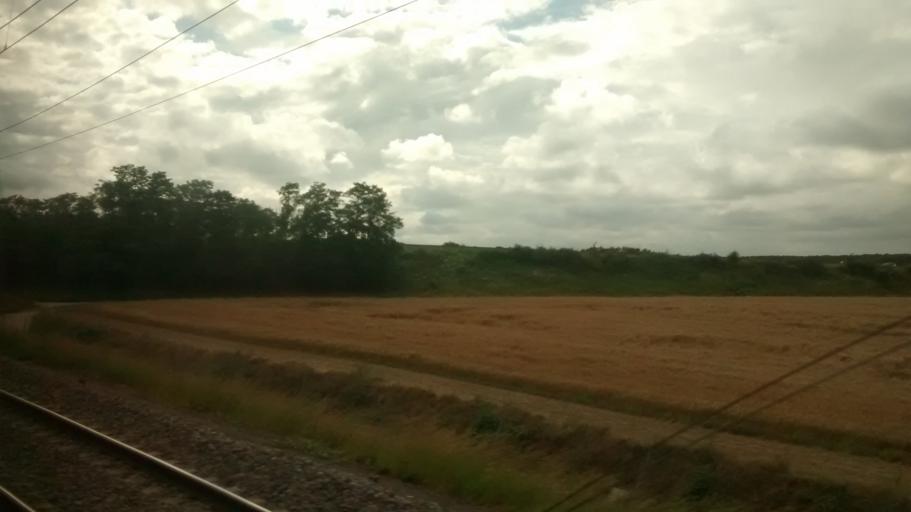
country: FR
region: Centre
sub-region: Departement d'Eure-et-Loir
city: Voves
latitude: 48.2482
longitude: 1.5460
